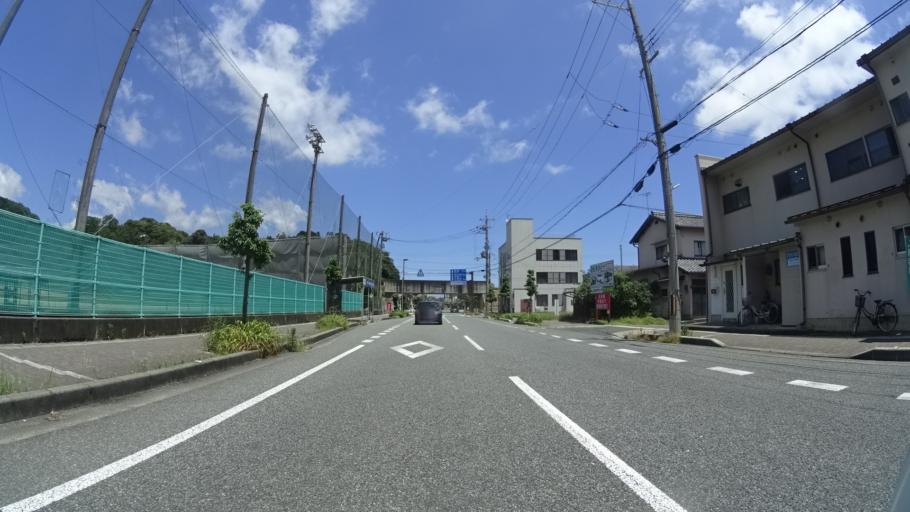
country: JP
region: Kyoto
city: Miyazu
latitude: 35.5288
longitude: 135.1909
